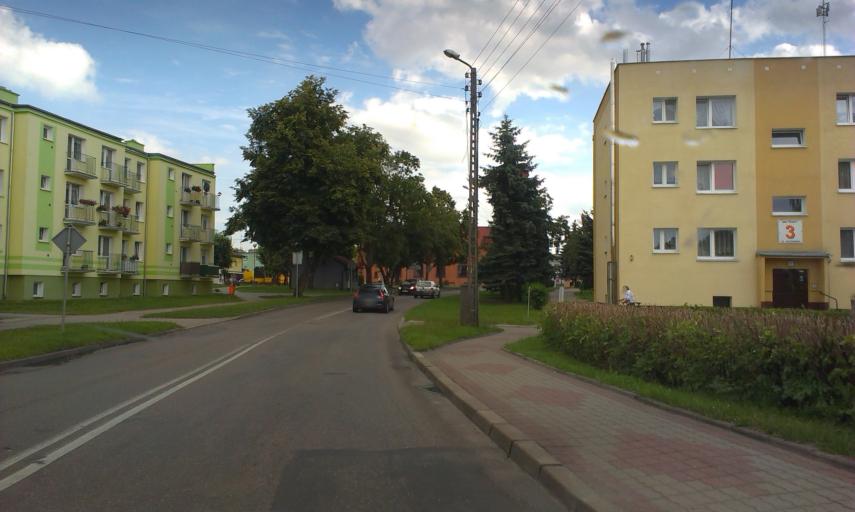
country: PL
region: Greater Poland Voivodeship
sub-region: Powiat zlotowski
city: Krajenka
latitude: 53.2984
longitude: 16.9909
